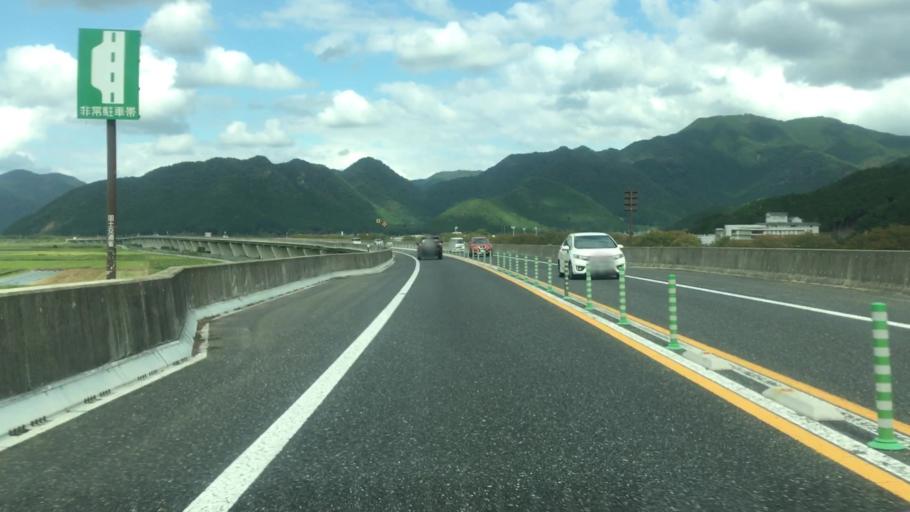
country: JP
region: Kyoto
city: Fukuchiyama
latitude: 35.1925
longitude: 135.0424
